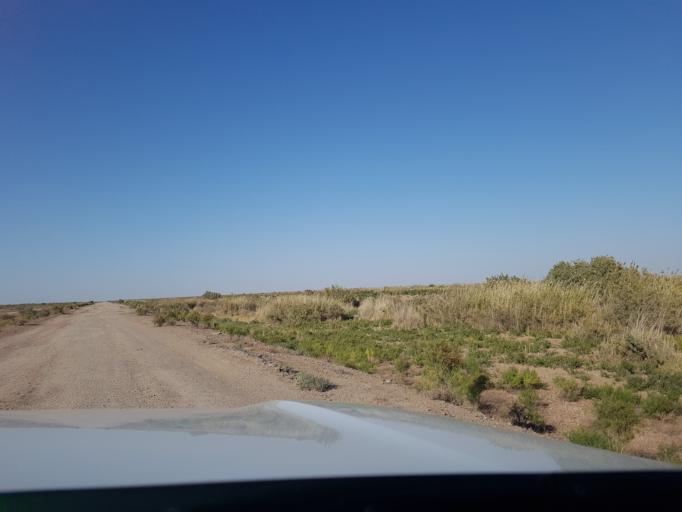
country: IR
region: Razavi Khorasan
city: Sarakhs
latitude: 36.9632
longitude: 61.3826
